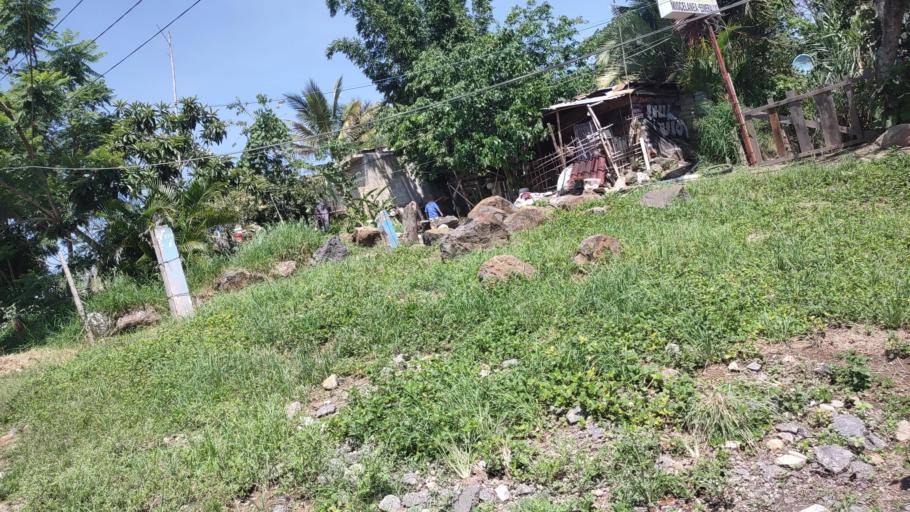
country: MX
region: Veracruz
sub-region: Emiliano Zapata
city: Dos Rios
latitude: 19.4909
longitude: -96.8161
